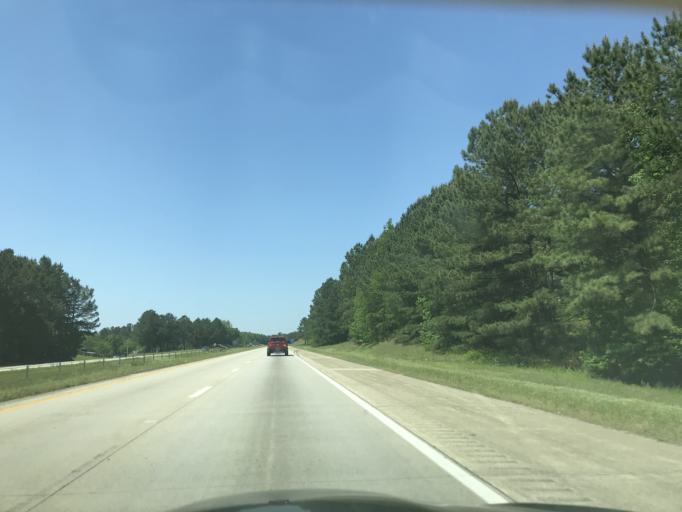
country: US
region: North Carolina
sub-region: Johnston County
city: Benson
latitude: 35.4323
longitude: -78.5324
